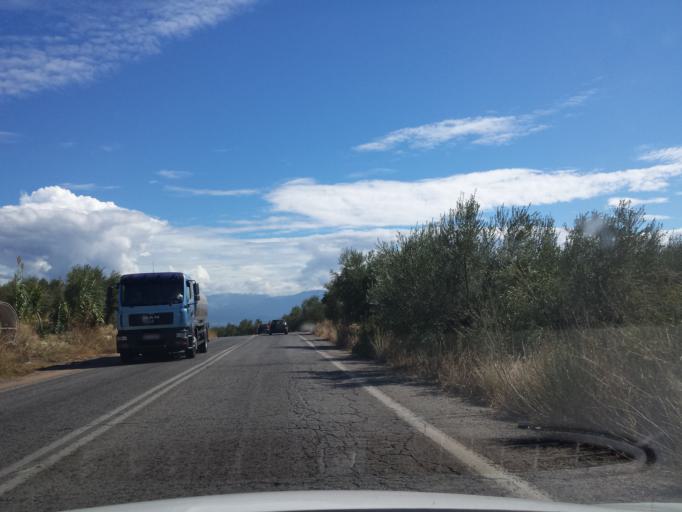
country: GR
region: Peloponnese
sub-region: Nomos Messinias
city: Messini
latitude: 37.0051
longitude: 21.9038
